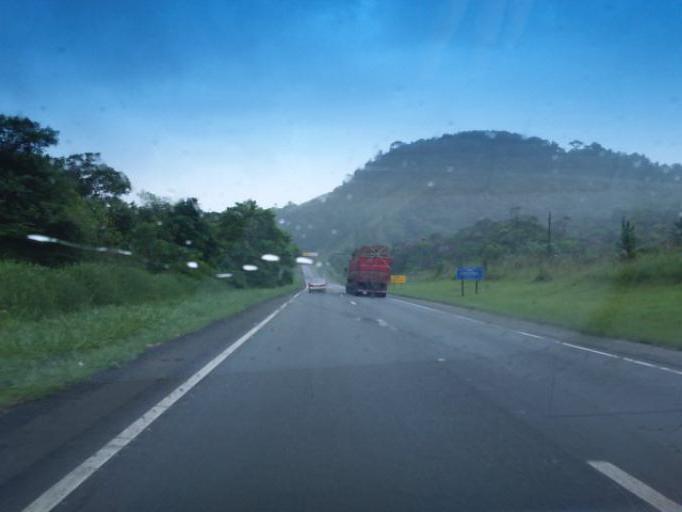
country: BR
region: Sao Paulo
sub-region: Cajati
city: Cajati
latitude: -24.8893
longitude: -48.2291
